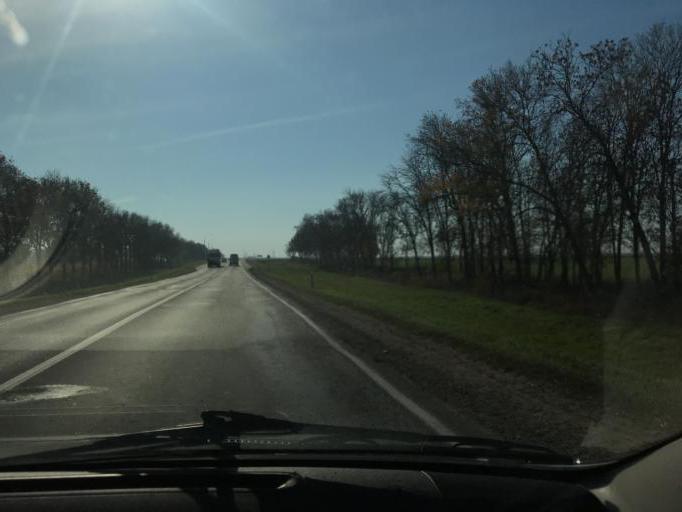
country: BY
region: Minsk
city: Salihorsk
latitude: 52.8761
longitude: 27.4674
